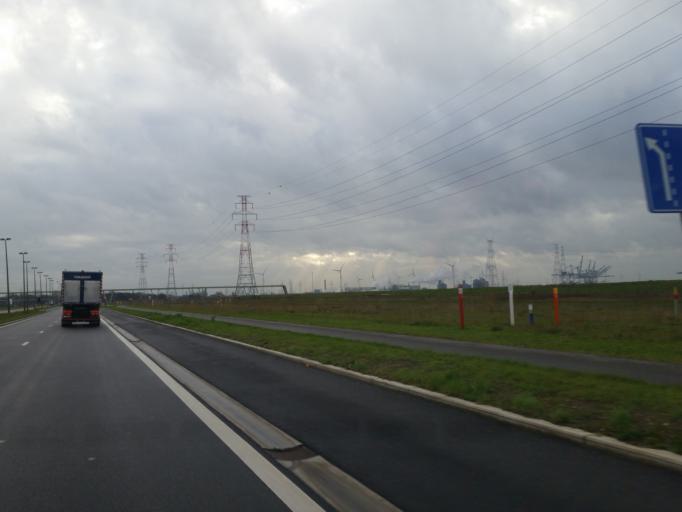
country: BE
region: Flanders
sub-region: Provincie Antwerpen
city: Stabroek
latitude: 51.3162
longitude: 4.2870
